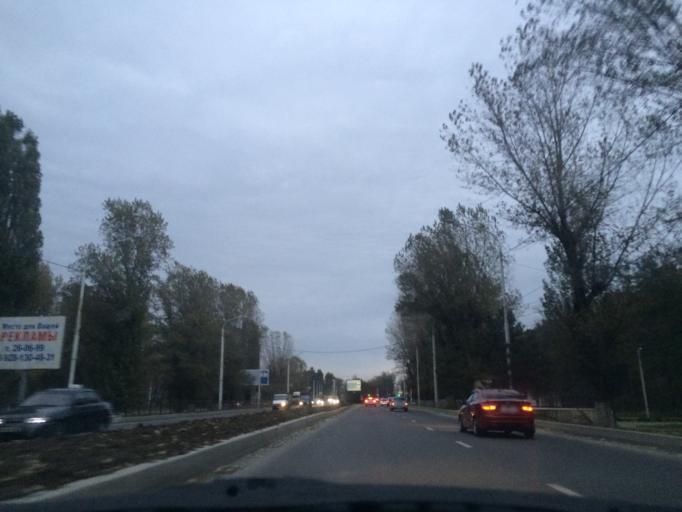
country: RU
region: Rostov
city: Novocherkassk
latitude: 47.4221
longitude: 40.0636
